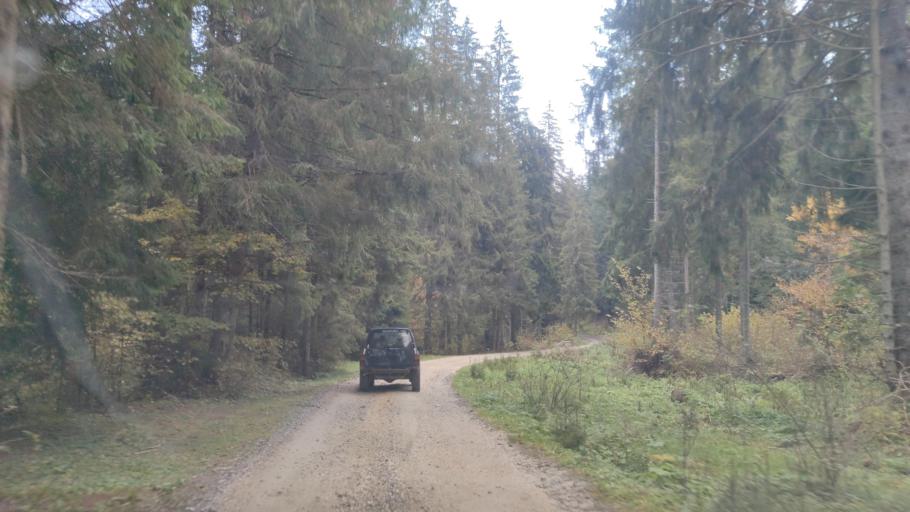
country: RO
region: Harghita
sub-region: Comuna Madaras
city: Madaras
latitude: 46.4814
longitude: 25.6611
